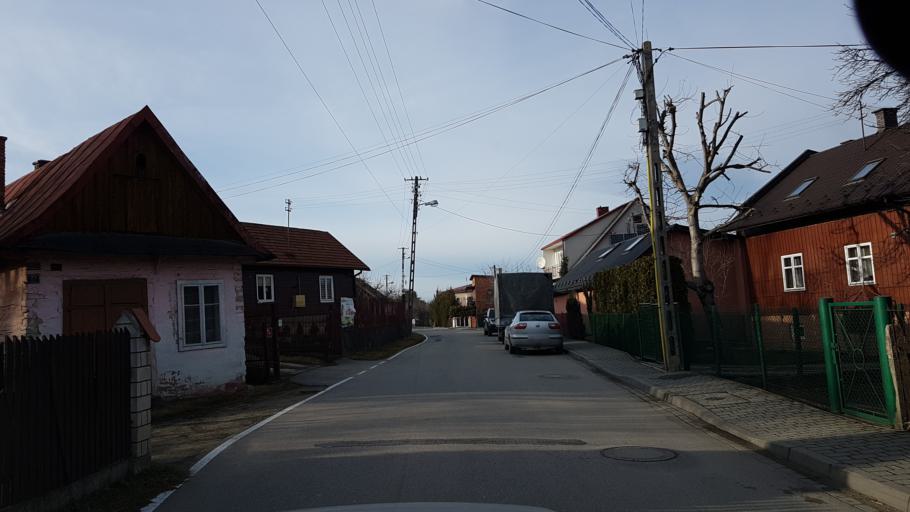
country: PL
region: Lesser Poland Voivodeship
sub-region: Powiat nowosadecki
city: Stary Sacz
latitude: 49.5392
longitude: 20.6548
